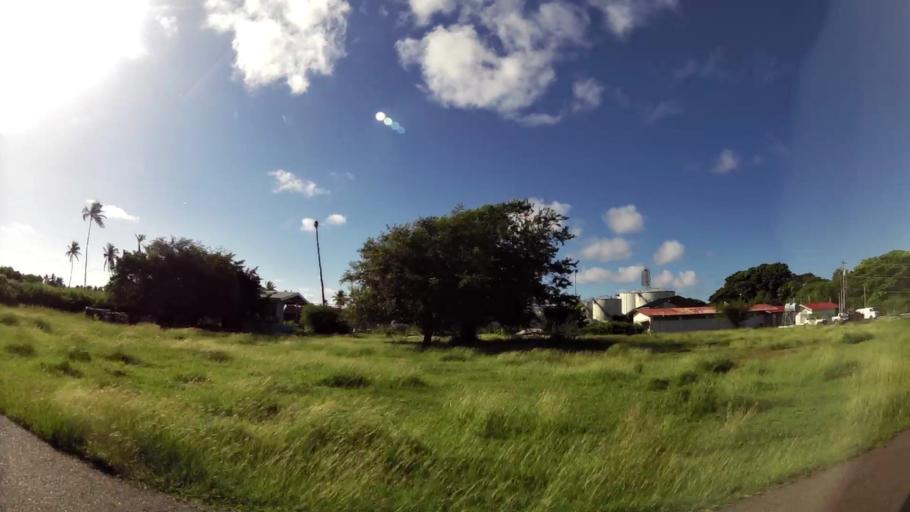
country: TT
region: Tobago
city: Scarborough
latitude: 11.1496
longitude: -60.8436
